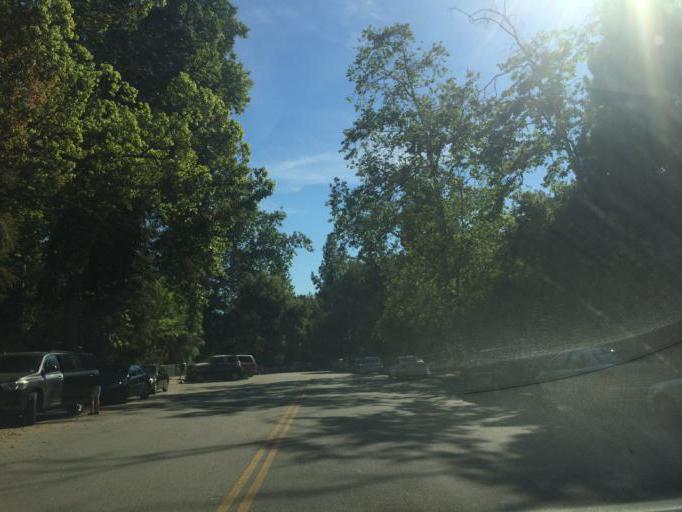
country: US
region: California
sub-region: Los Angeles County
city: Hollywood
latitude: 34.1144
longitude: -118.3073
